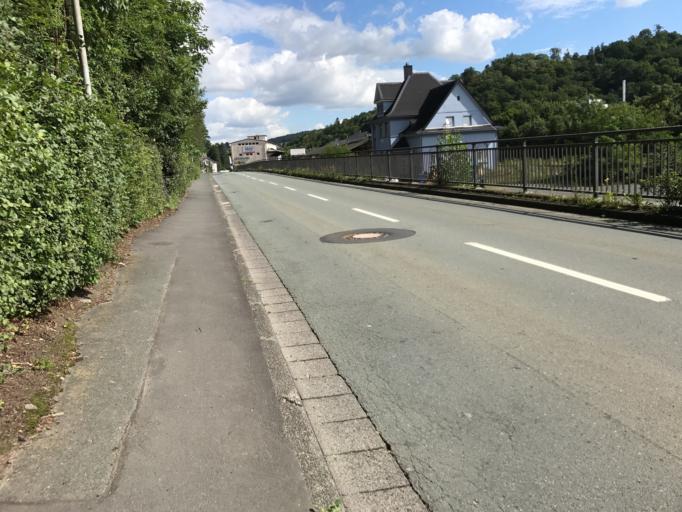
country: DE
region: Hesse
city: Weilburg
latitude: 50.4878
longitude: 8.2677
